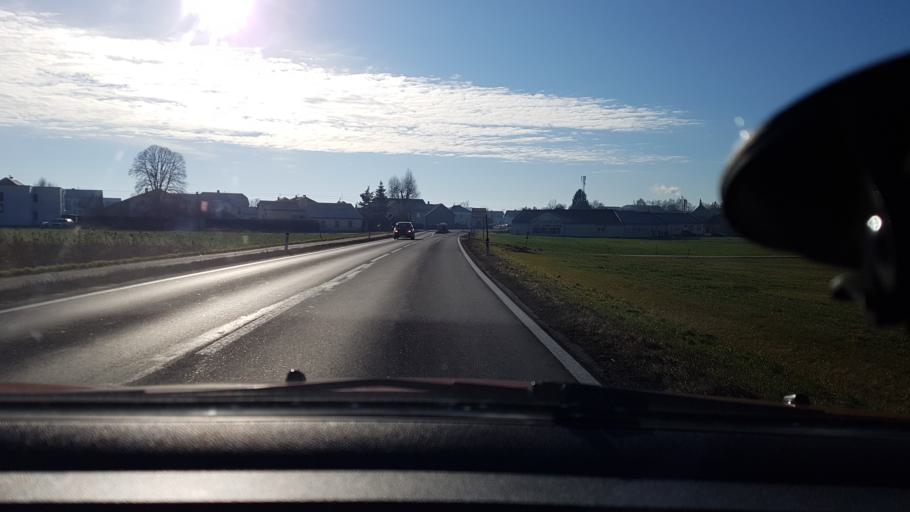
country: AT
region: Upper Austria
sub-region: Politischer Bezirk Braunau am Inn
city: Braunau am Inn
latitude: 48.1821
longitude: 13.0543
